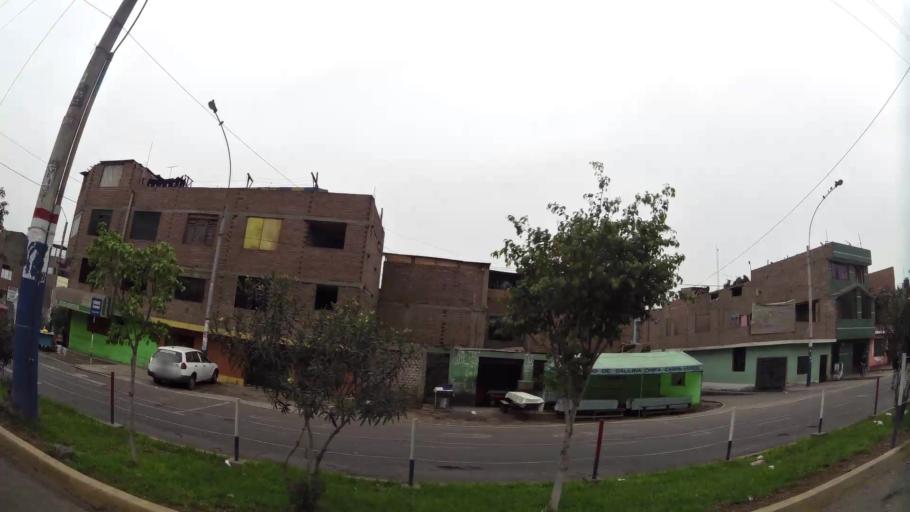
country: PE
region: Lima
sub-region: Lima
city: Independencia
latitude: -11.9654
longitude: -77.0094
